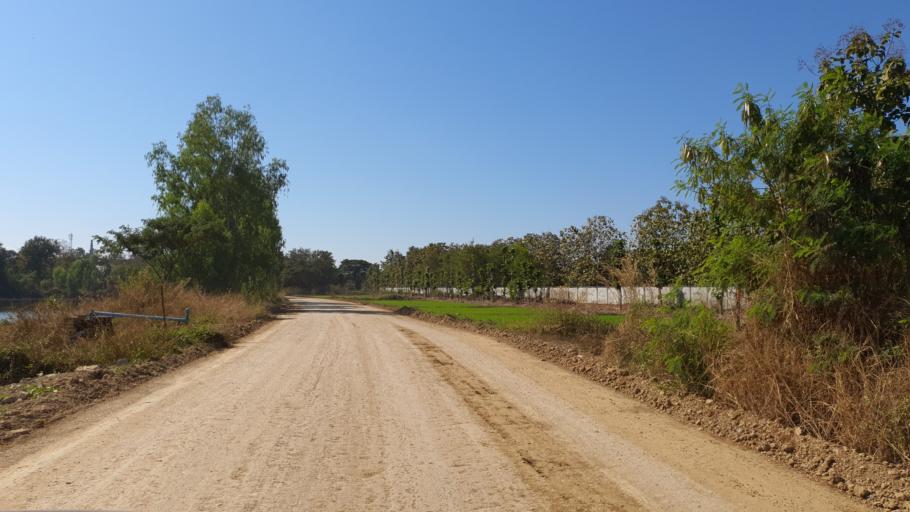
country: TH
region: Lamphun
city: Ban Thi
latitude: 18.6652
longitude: 99.1057
